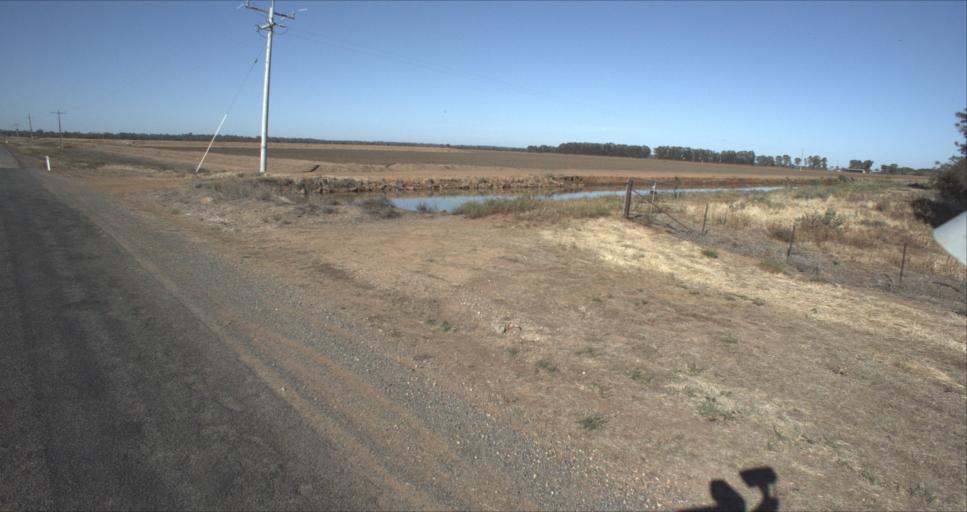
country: AU
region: New South Wales
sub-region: Leeton
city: Leeton
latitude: -34.5880
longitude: 146.2602
